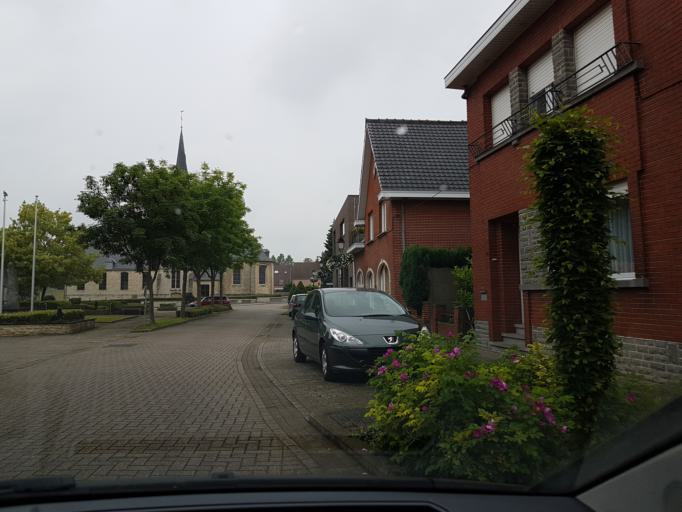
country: BE
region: Flanders
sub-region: Provincie Vlaams-Brabant
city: Zaventem
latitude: 50.8804
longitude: 4.5030
